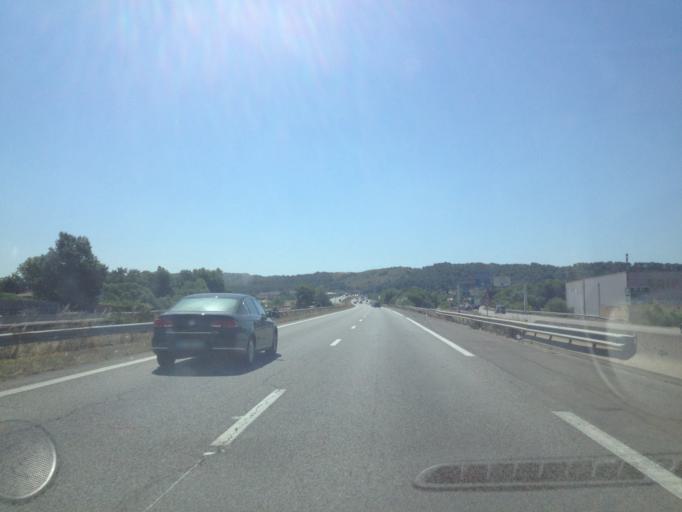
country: FR
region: Provence-Alpes-Cote d'Azur
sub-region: Departement des Bouches-du-Rhone
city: Saint-Victoret
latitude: 43.4199
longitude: 5.2706
